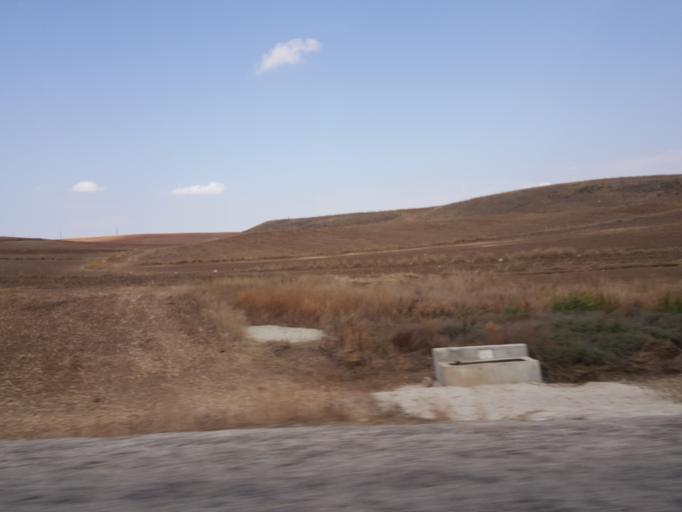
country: TR
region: Corum
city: Alaca
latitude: 40.1560
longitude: 34.7497
